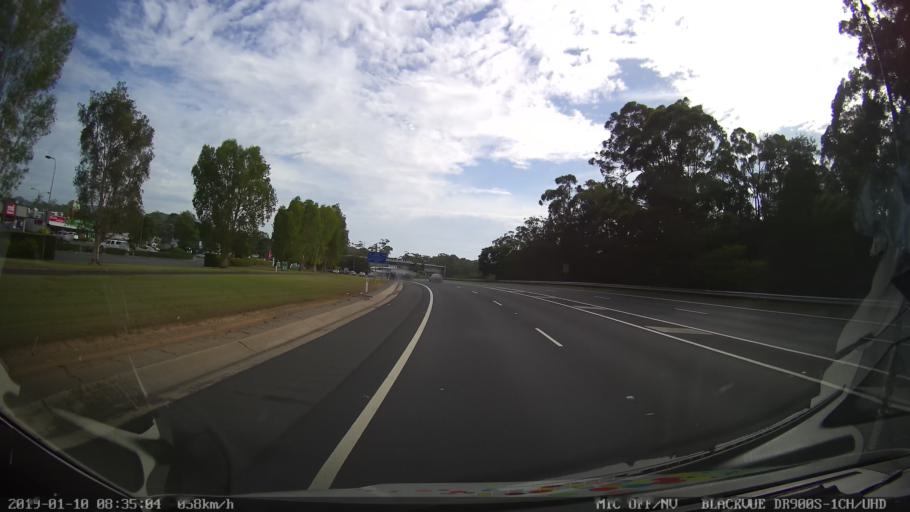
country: AU
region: New South Wales
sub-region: Coffs Harbour
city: Boambee
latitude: -30.3187
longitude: 153.0899
